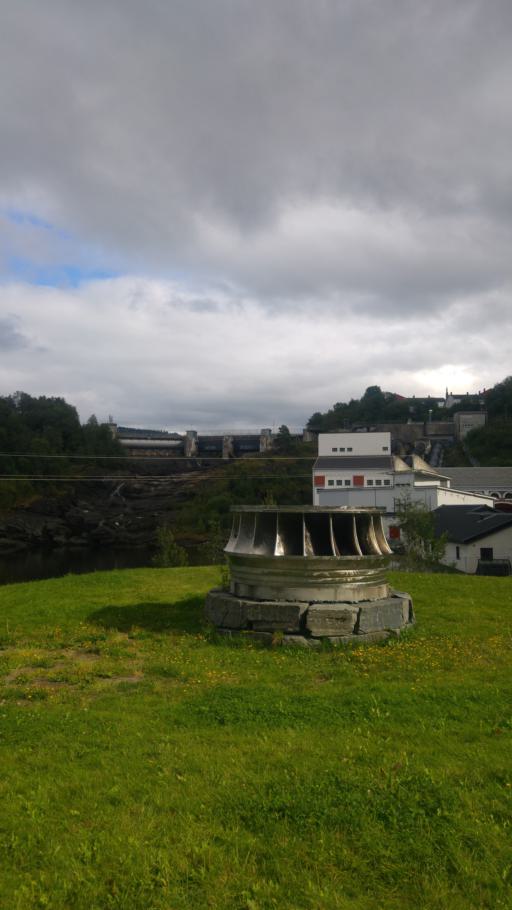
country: NO
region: Sor-Trondelag
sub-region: Trondheim
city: Trondheim
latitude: 63.3737
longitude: 10.4049
